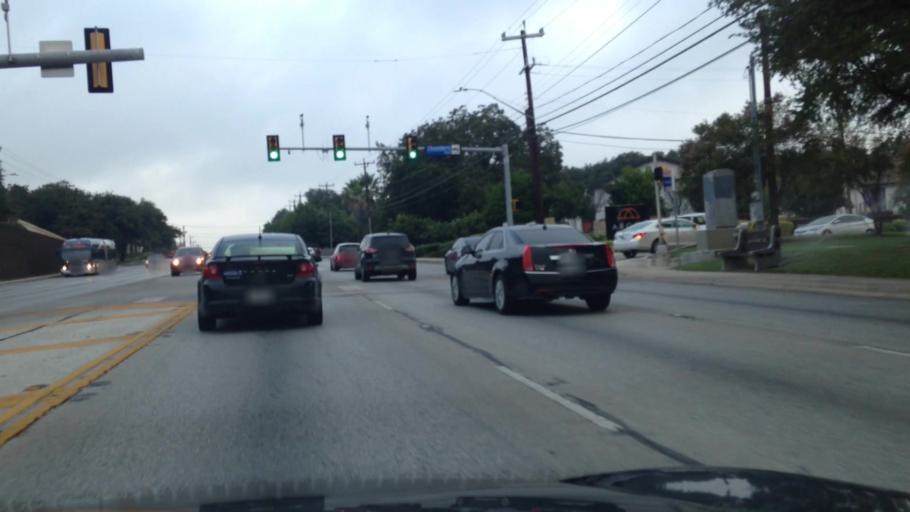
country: US
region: Texas
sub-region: Bexar County
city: Balcones Heights
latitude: 29.5074
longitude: -98.5641
